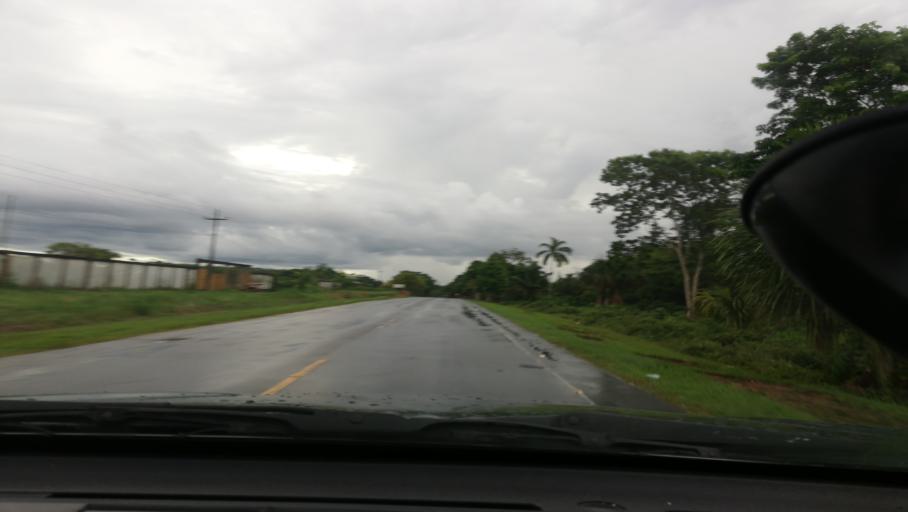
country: PE
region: Loreto
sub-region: Provincia de Maynas
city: Iquitos
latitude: -3.9039
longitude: -73.3564
